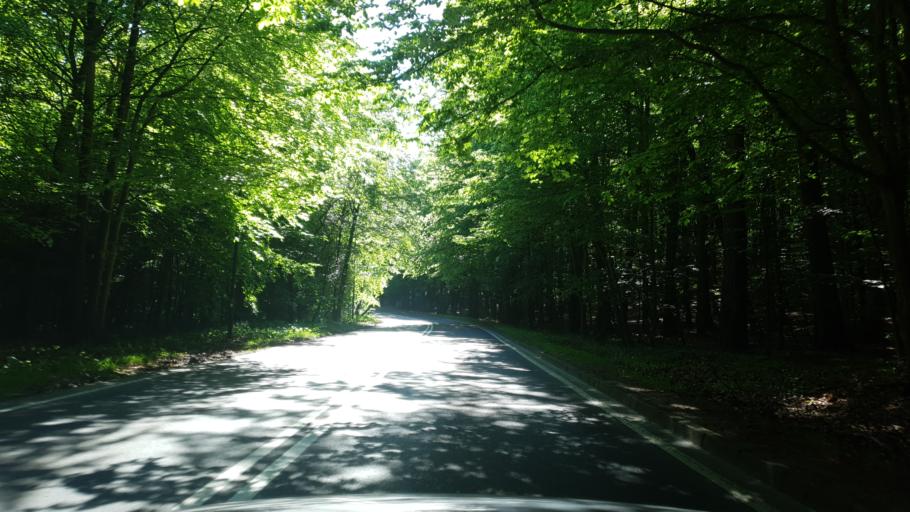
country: PL
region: Pomeranian Voivodeship
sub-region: Sopot
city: Sopot
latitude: 54.4563
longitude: 18.5247
